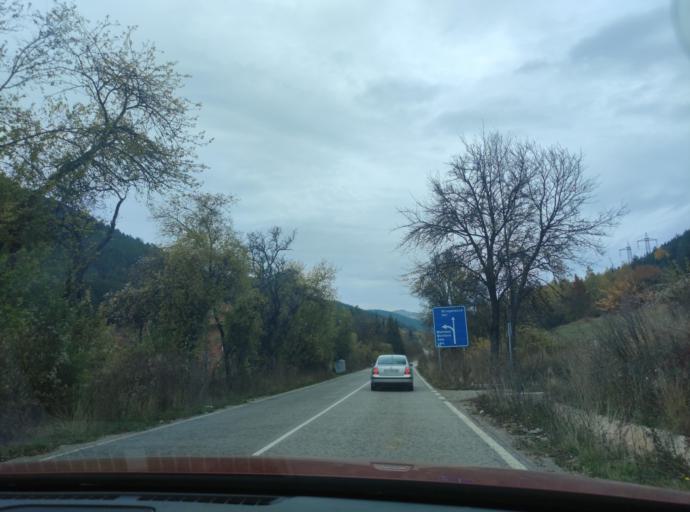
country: BG
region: Sofiya
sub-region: Obshtina Godech
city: Godech
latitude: 43.0369
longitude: 23.1371
